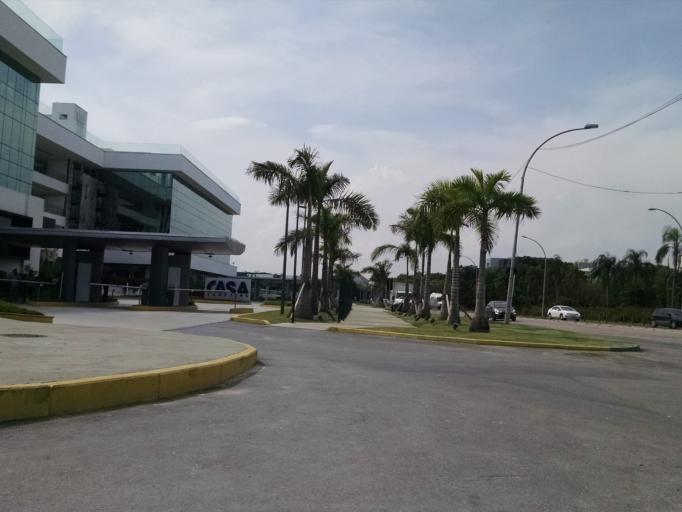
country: BR
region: Rio de Janeiro
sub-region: Rio De Janeiro
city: Rio de Janeiro
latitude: -22.9937
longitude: -43.3614
